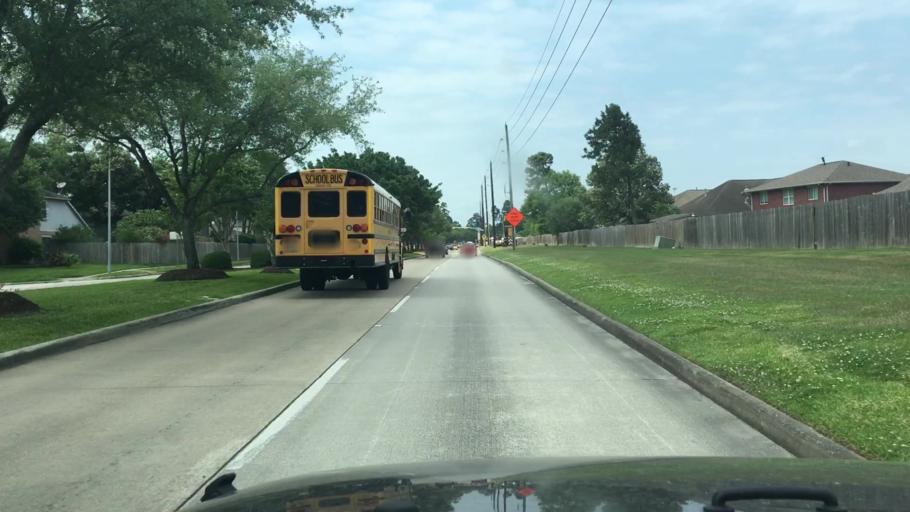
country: US
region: Texas
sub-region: Harris County
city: Atascocita
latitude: 29.9707
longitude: -95.2115
